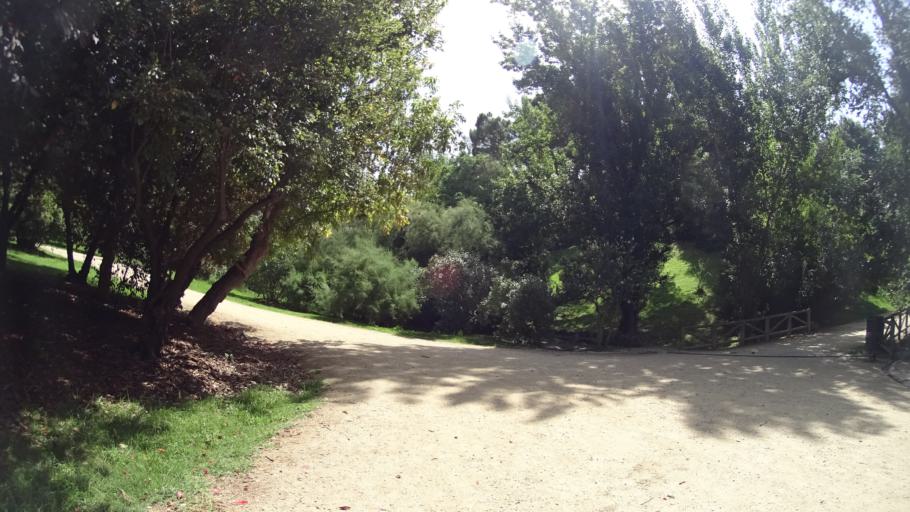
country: ES
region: Madrid
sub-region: Provincia de Madrid
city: Moncloa-Aravaca
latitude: 40.4346
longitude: -3.7250
